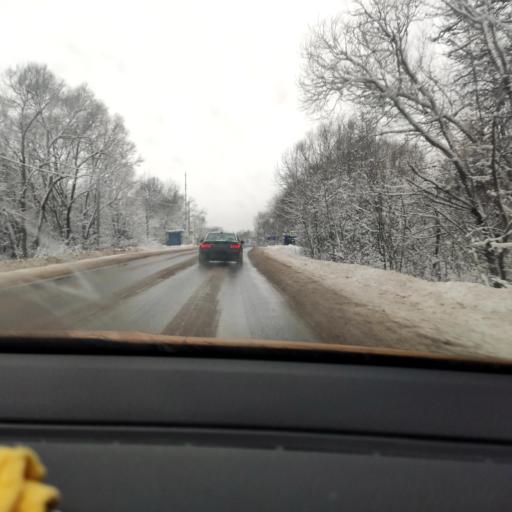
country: RU
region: Moskovskaya
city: Yershovo
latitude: 55.7628
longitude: 36.8622
